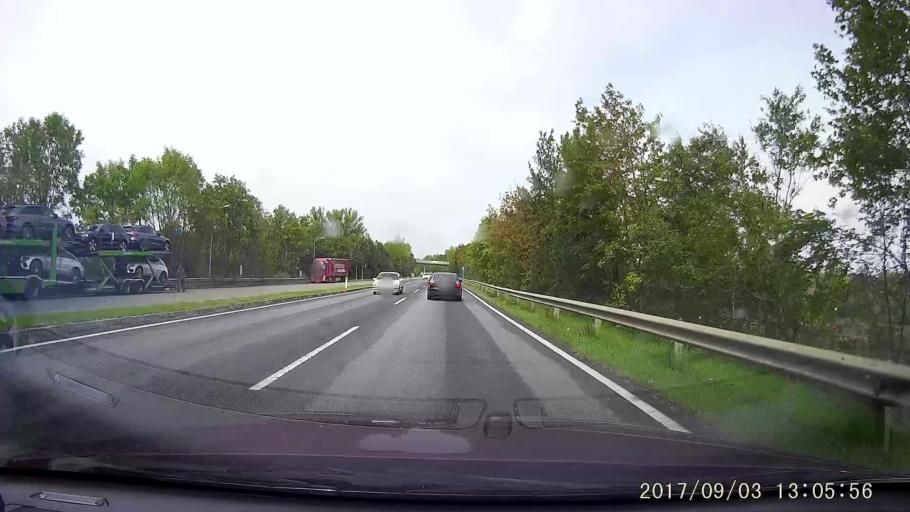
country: AT
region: Lower Austria
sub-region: Politischer Bezirk Hollabrunn
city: Hollabrunn
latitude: 48.5641
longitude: 16.0644
